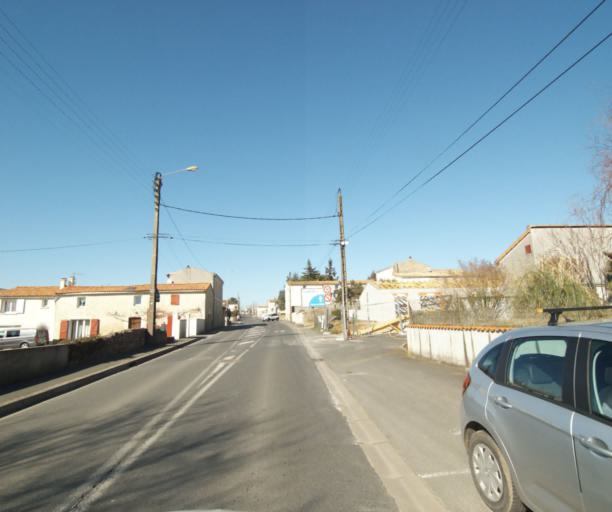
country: FR
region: Poitou-Charentes
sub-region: Departement des Deux-Sevres
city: Niort
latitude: 46.3495
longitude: -0.4778
